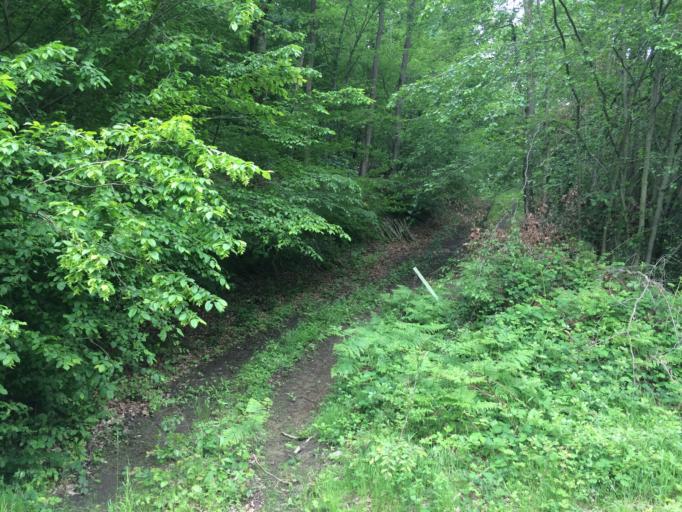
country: BE
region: Wallonia
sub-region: Province de Namur
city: Yvoir
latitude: 50.3254
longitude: 4.9505
